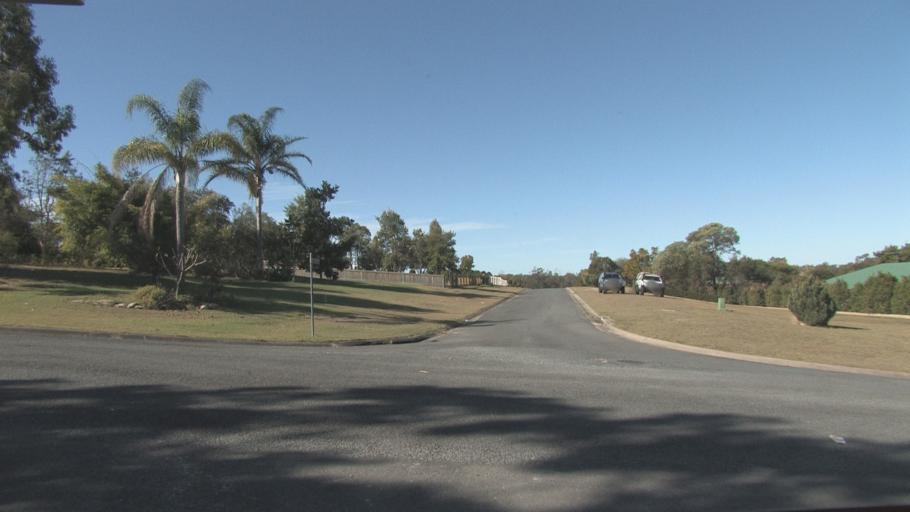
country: AU
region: Queensland
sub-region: Ipswich
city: Springfield Lakes
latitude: -27.7303
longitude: 152.9418
